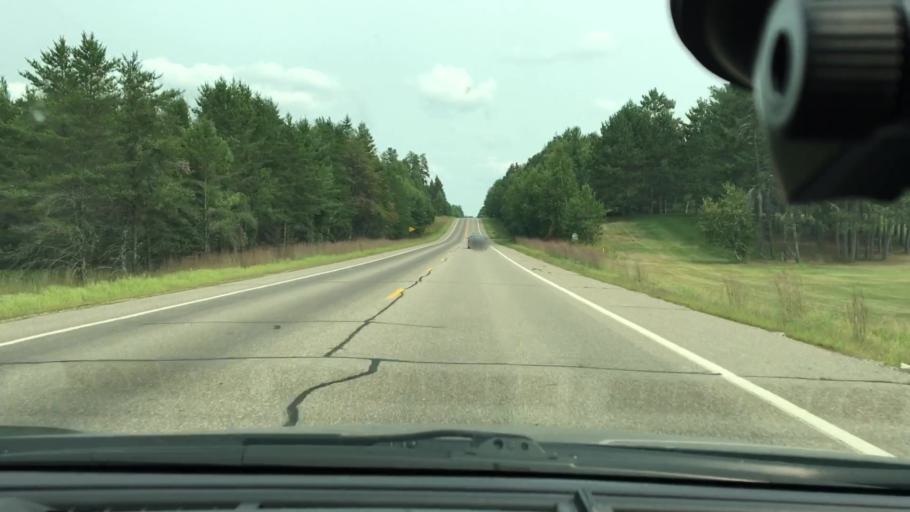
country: US
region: Minnesota
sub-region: Crow Wing County
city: Cross Lake
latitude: 46.7309
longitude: -93.9848
